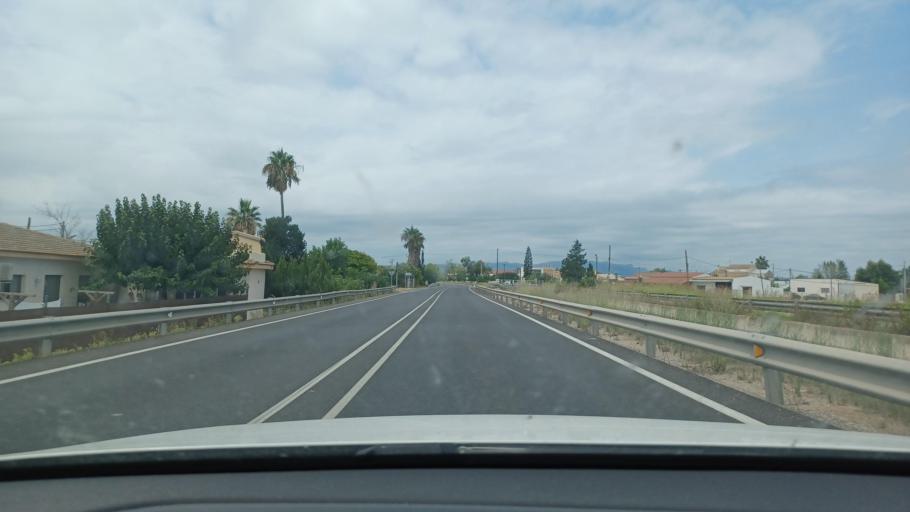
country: ES
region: Catalonia
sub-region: Provincia de Tarragona
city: Deltebre
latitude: 40.7174
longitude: 0.7504
